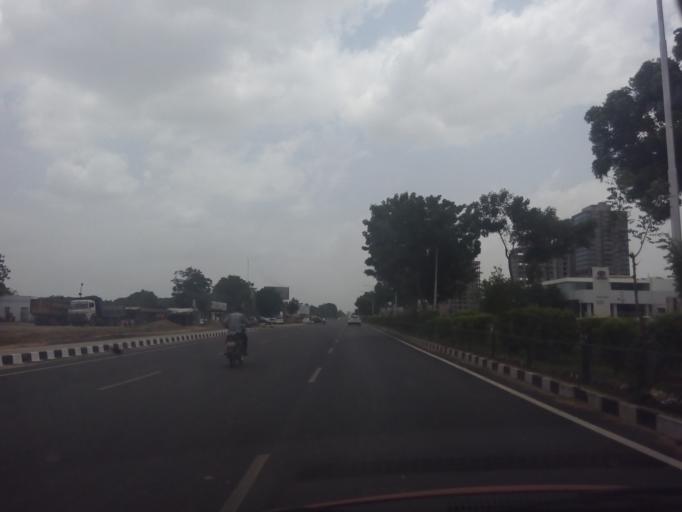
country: IN
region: Gujarat
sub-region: Ahmadabad
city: Sarkhej
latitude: 23.0001
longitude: 72.4988
